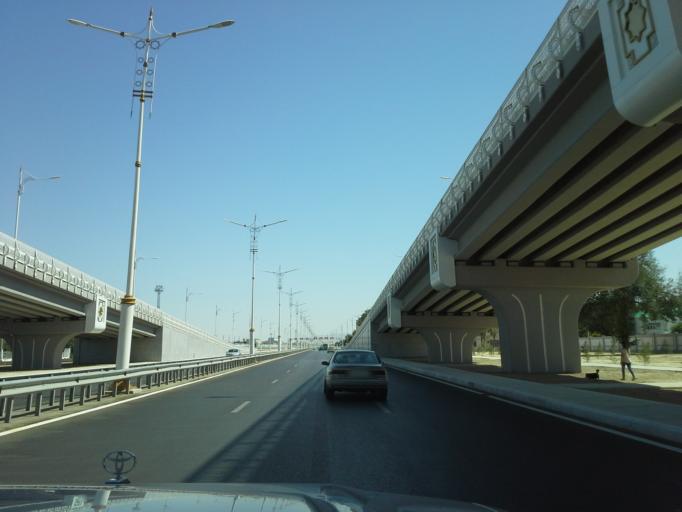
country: TM
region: Ahal
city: Ashgabat
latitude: 37.9400
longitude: 58.4017
